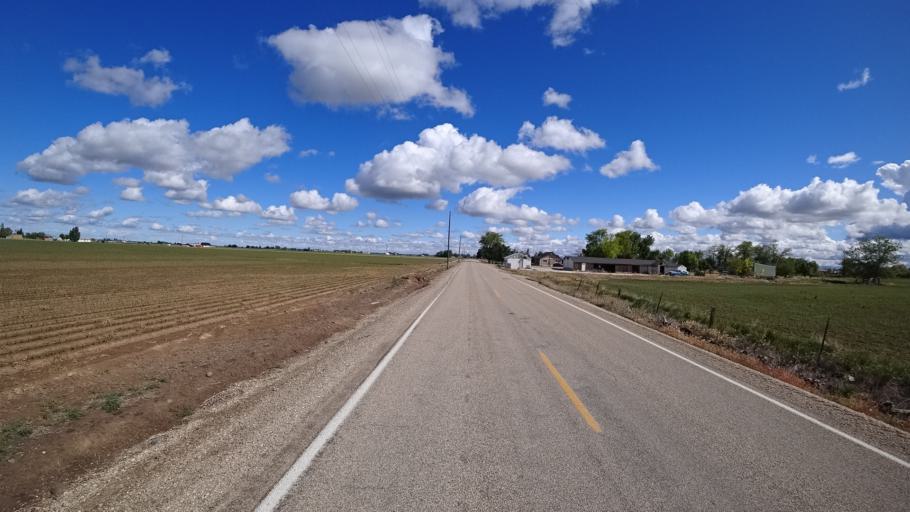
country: US
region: Idaho
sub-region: Ada County
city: Kuna
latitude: 43.4710
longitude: -116.4537
